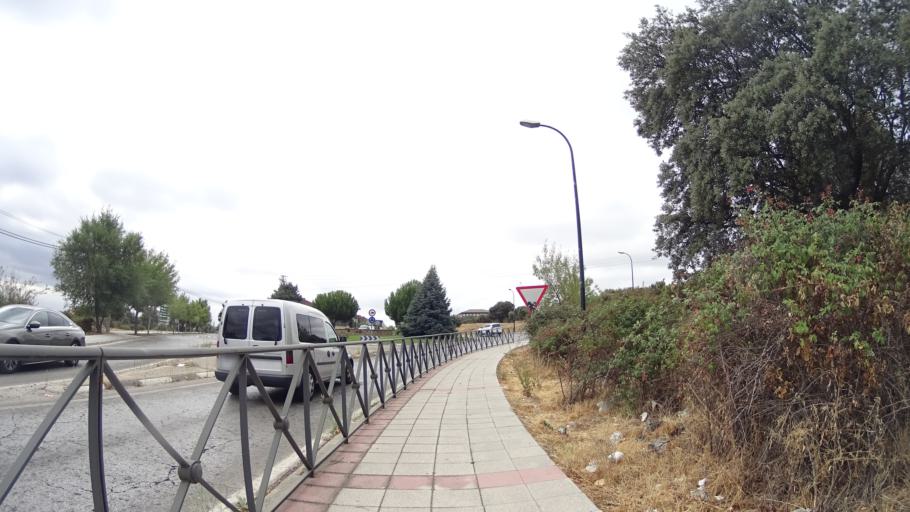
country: ES
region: Madrid
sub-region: Provincia de Madrid
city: Galapagar
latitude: 40.5855
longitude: -4.0117
